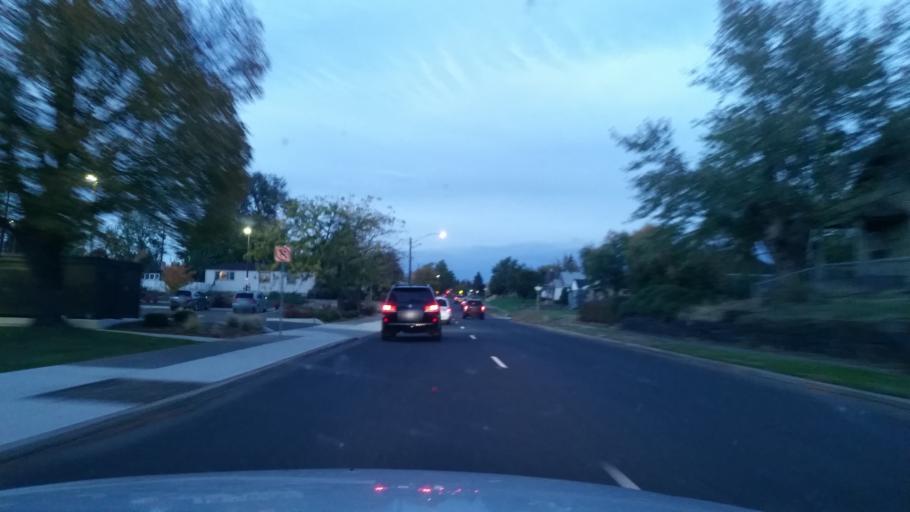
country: US
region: Washington
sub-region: Spokane County
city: Spokane
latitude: 47.6937
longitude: -117.4351
